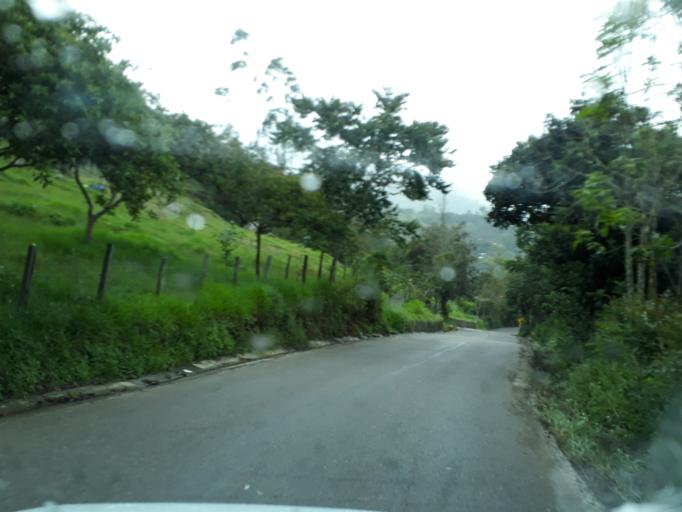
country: CO
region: Cundinamarca
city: Gacheta
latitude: 4.8229
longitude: -73.6653
